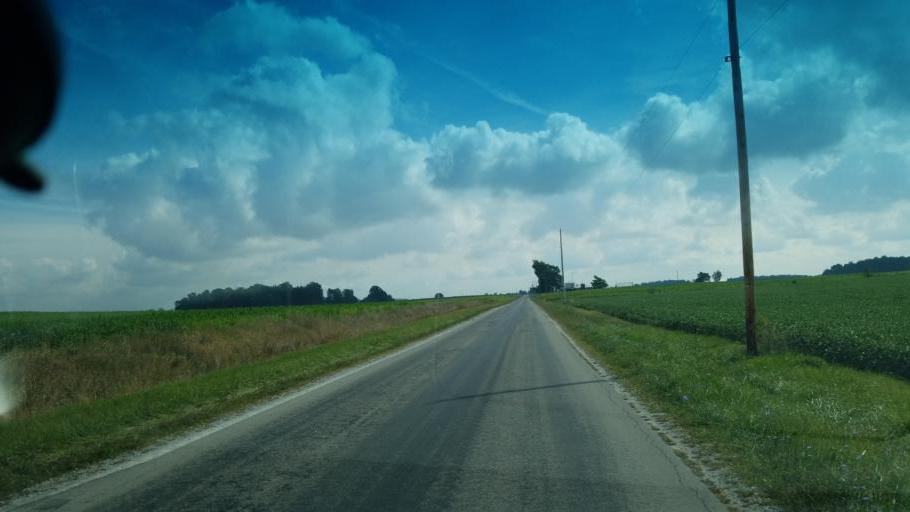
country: US
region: Ohio
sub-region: Hardin County
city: Forest
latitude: 40.8615
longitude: -83.4432
